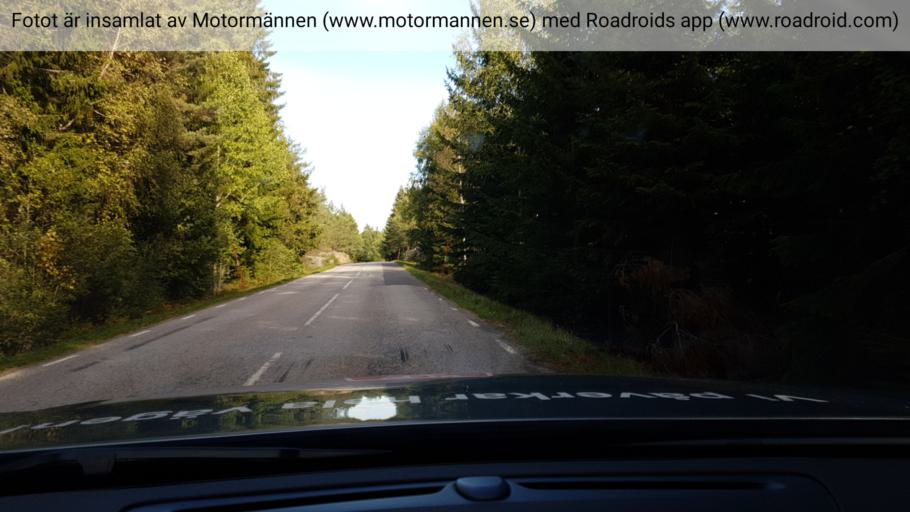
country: SE
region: Kalmar
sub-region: Vasterviks Kommun
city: Forserum
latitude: 58.0284
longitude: 16.5840
